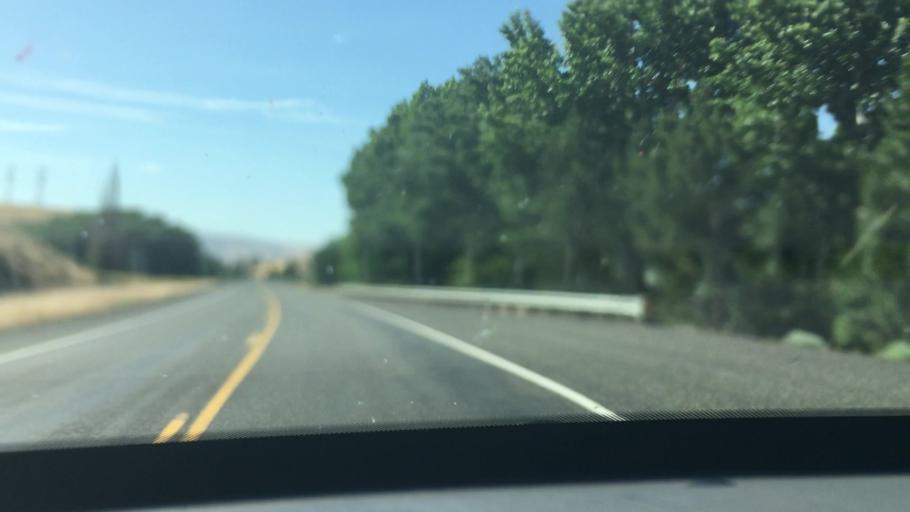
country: US
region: Oregon
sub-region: Sherman County
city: Moro
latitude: 45.6199
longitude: -120.7395
